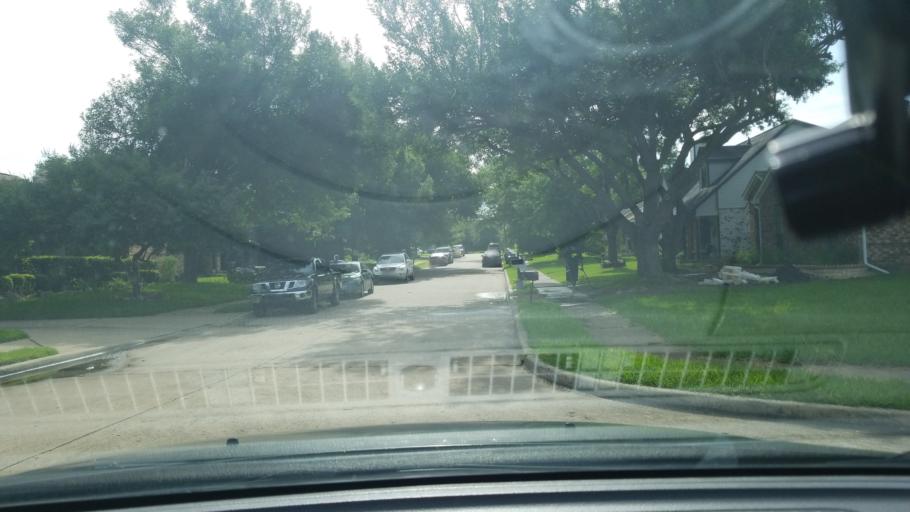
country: US
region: Texas
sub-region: Dallas County
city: Balch Springs
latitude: 32.7752
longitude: -96.6620
